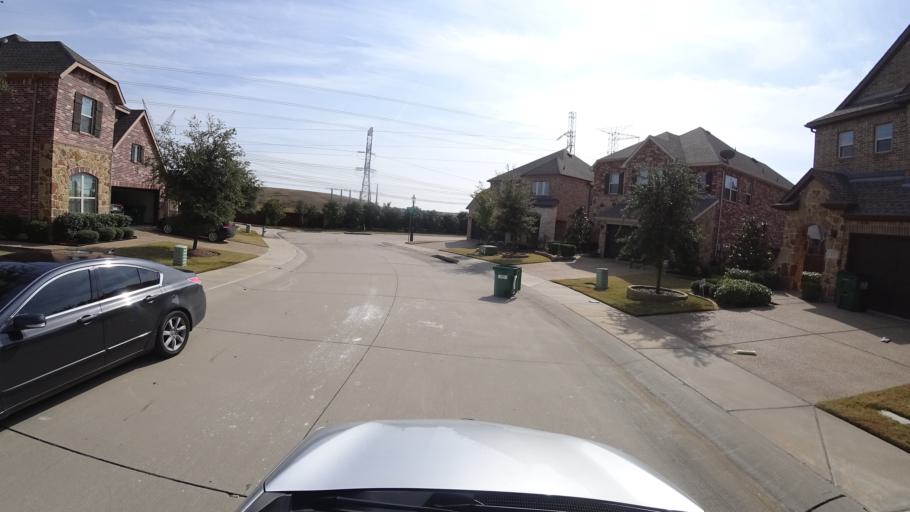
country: US
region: Texas
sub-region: Denton County
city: The Colony
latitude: 33.0559
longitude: -96.9010
